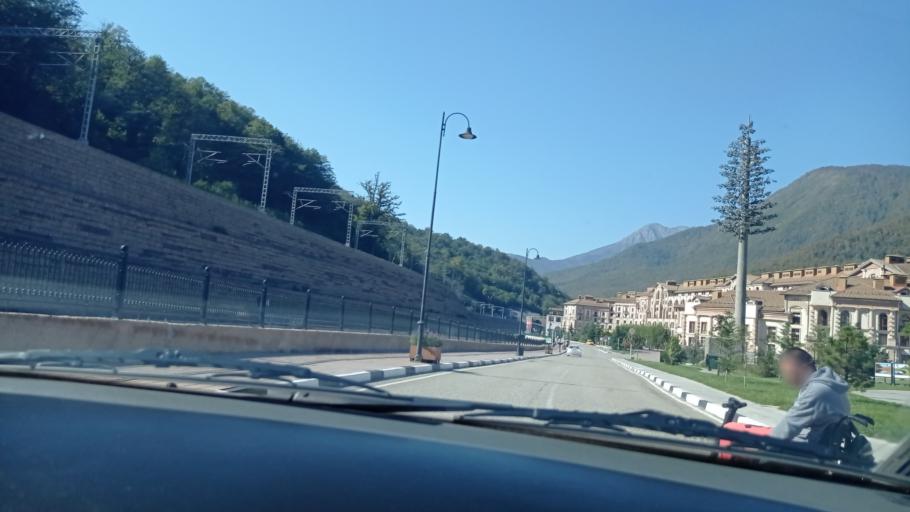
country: RU
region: Krasnodarskiy
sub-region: Sochi City
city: Krasnaya Polyana
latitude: 43.6819
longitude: 40.2628
